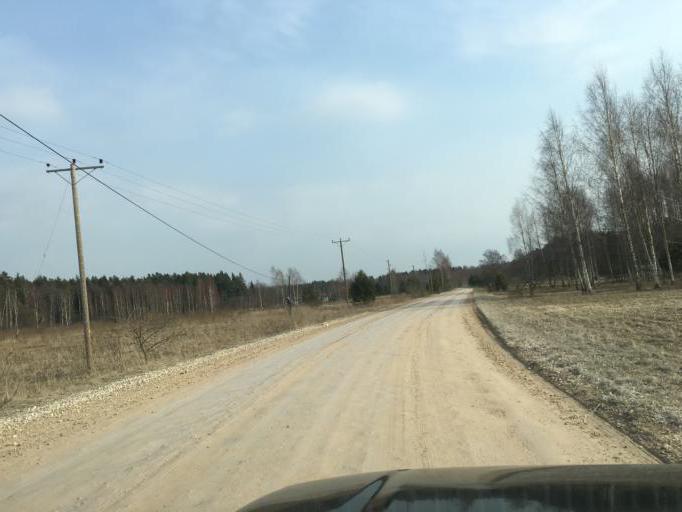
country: LV
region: Olaine
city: Olaine
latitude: 56.7925
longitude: 23.9907
